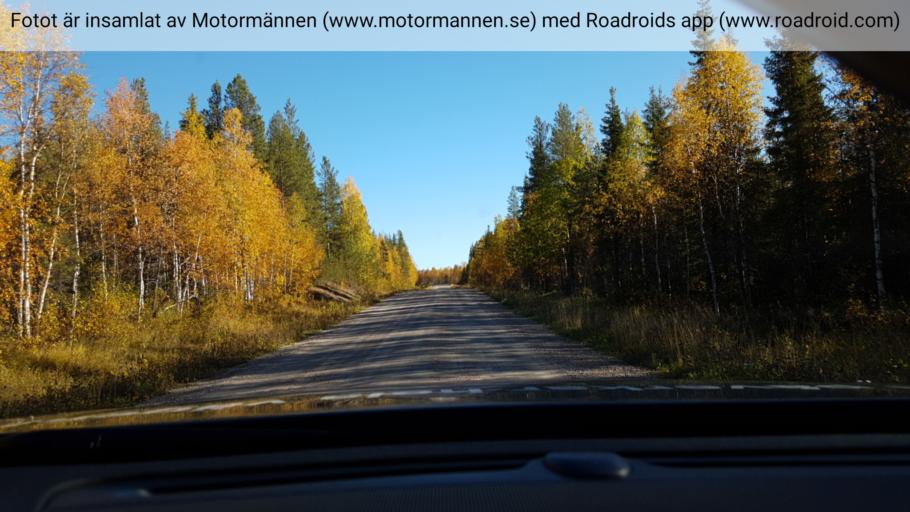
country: SE
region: Norrbotten
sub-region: Gallivare Kommun
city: Gaellivare
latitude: 66.5160
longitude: 20.9180
